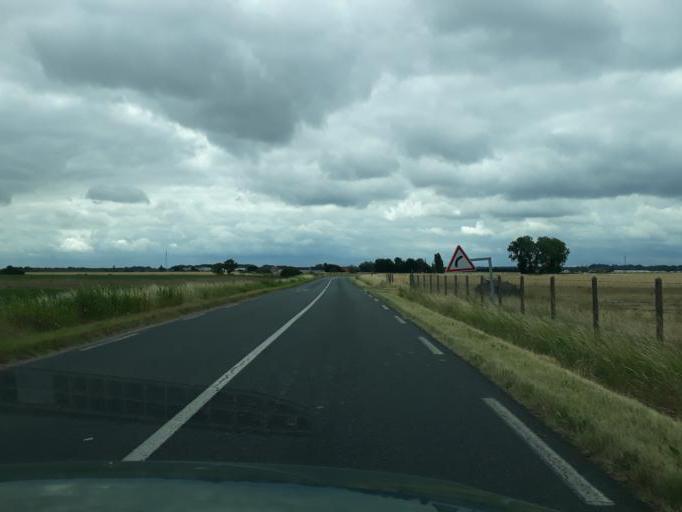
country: FR
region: Centre
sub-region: Departement du Loiret
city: Saint-Denis-en-Val
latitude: 47.8653
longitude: 1.9455
